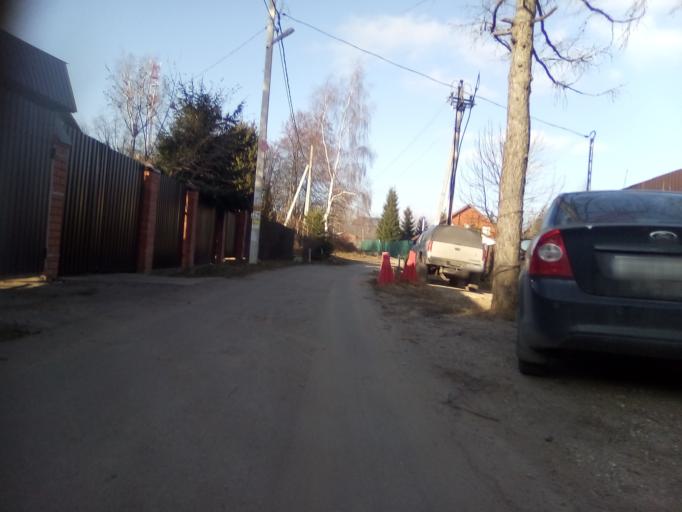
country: RU
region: Moskovskaya
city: Gorki Vtoryye
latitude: 55.6886
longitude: 37.1405
